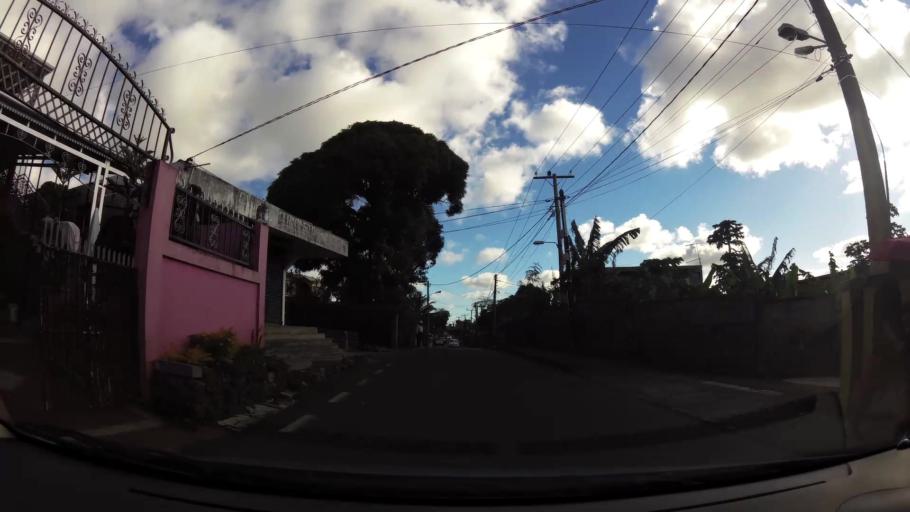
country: MU
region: Plaines Wilhems
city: Curepipe
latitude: -20.2970
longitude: 57.5118
